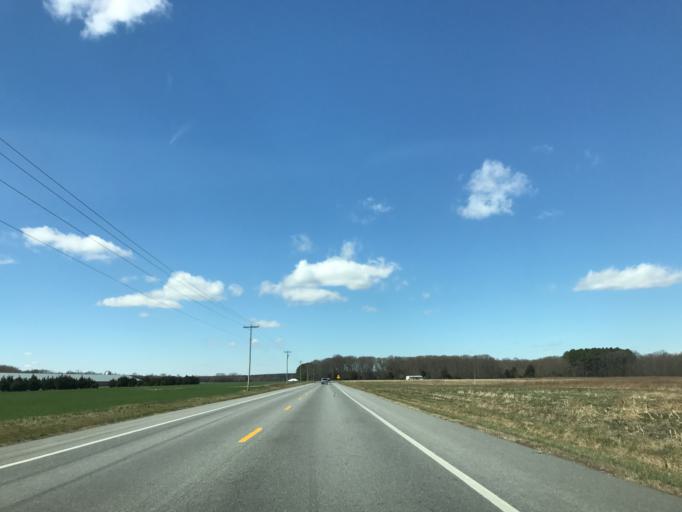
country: US
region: Maryland
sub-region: Caroline County
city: Ridgely
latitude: 39.1030
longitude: -75.8934
